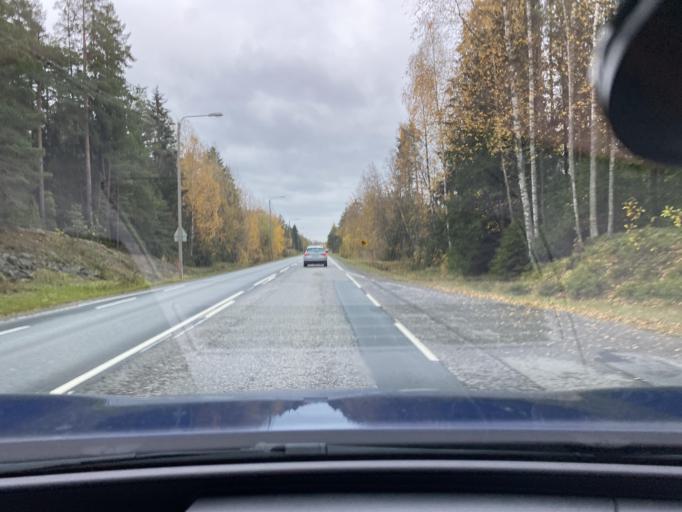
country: FI
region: Varsinais-Suomi
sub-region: Vakka-Suomi
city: Pyhaeranta
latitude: 60.9944
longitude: 21.5772
